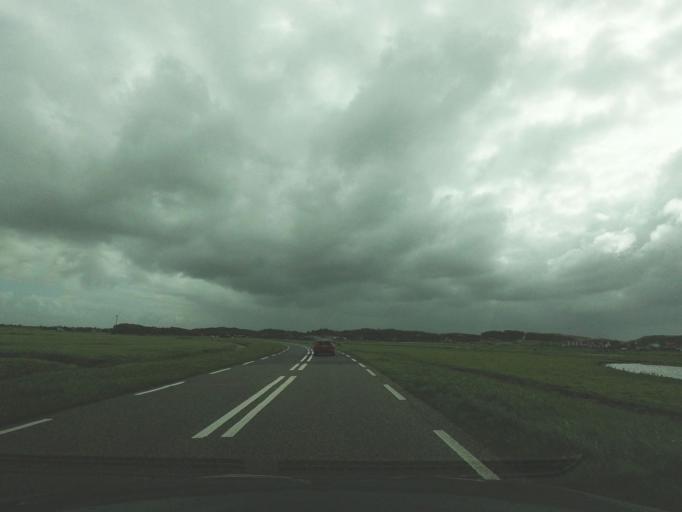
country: NL
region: North Holland
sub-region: Gemeente Bergen
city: Egmond aan Zee
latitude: 52.7310
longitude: 4.6450
